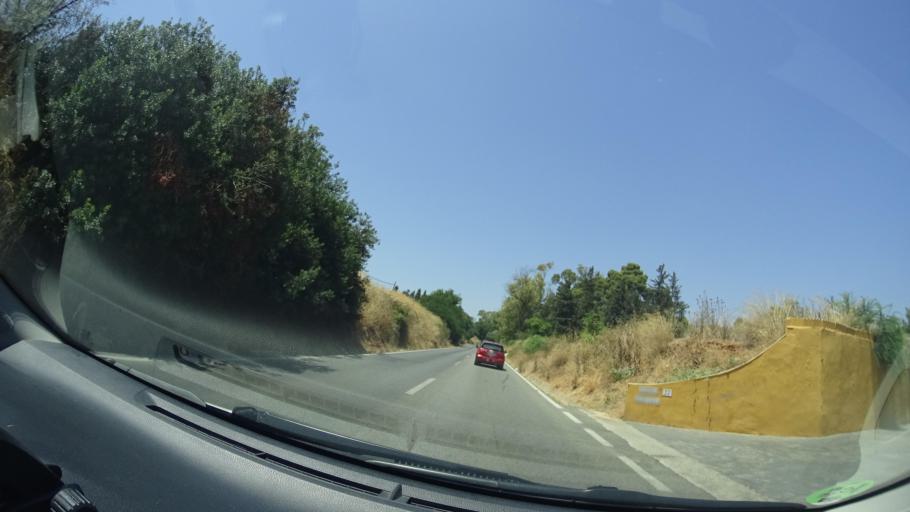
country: ES
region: Andalusia
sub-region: Provincia de Cadiz
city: Jerez de la Frontera
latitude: 36.6683
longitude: -6.1182
